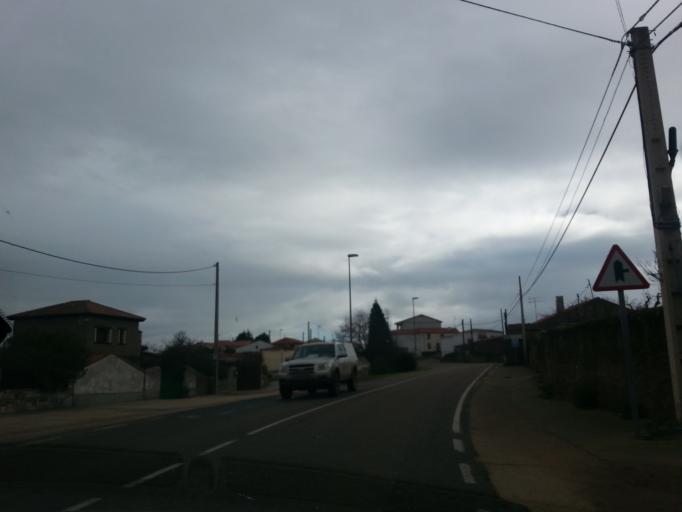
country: ES
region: Castille and Leon
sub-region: Provincia de Salamanca
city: Tamames
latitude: 40.6558
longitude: -6.1021
